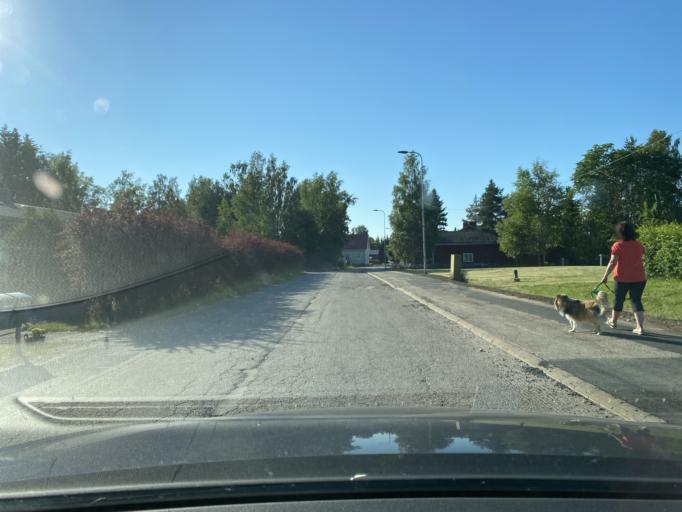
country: FI
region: Satakunta
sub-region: Pori
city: Huittinen
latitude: 61.1699
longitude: 22.7002
